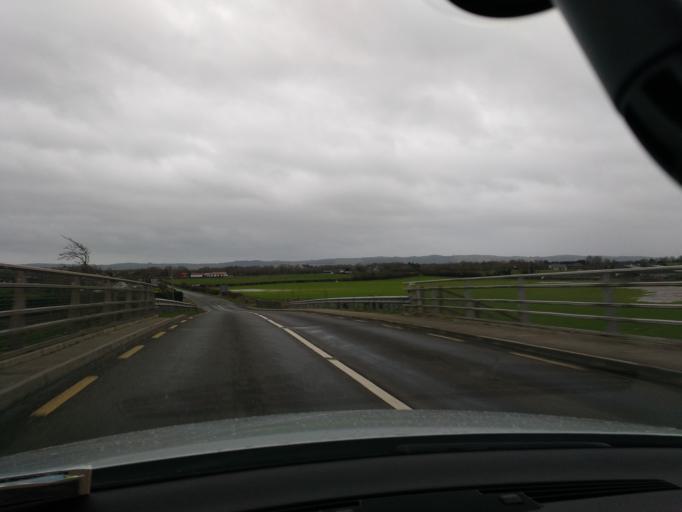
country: IE
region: Munster
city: Thurles
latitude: 52.6715
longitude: -7.6925
